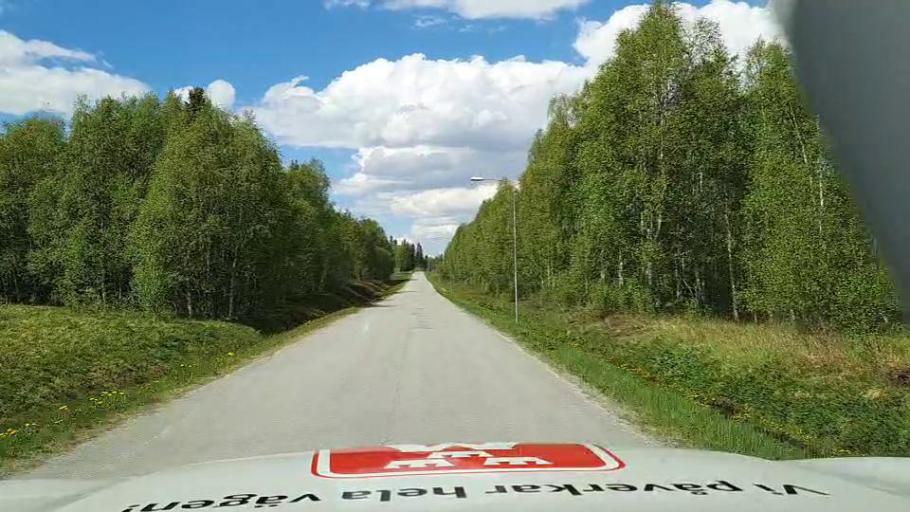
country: NO
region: Nord-Trondelag
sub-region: Lierne
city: Sandvika
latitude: 64.1177
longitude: 14.1460
